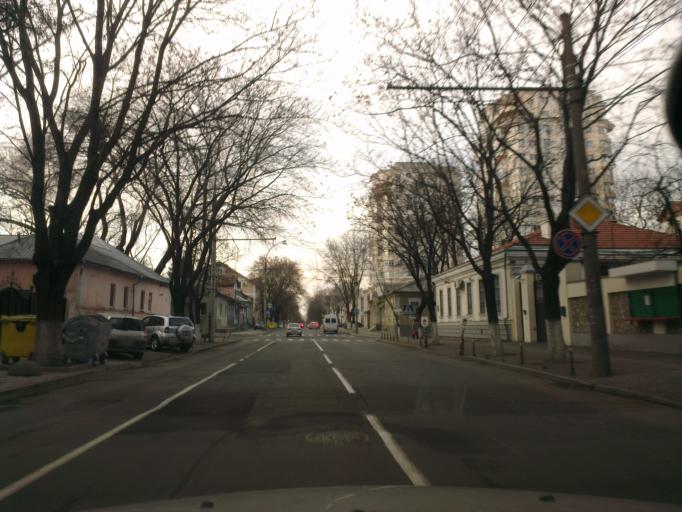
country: MD
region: Chisinau
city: Chisinau
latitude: 47.0251
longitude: 28.8229
